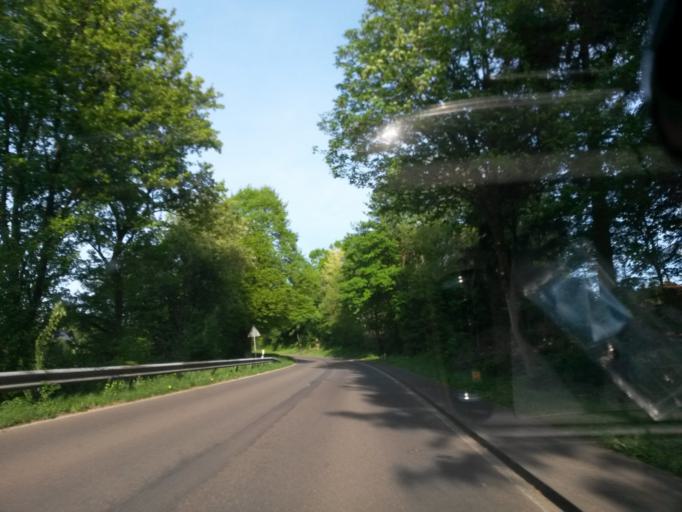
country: DE
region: North Rhine-Westphalia
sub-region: Regierungsbezirk Koln
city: Much
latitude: 50.9427
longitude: 7.4451
